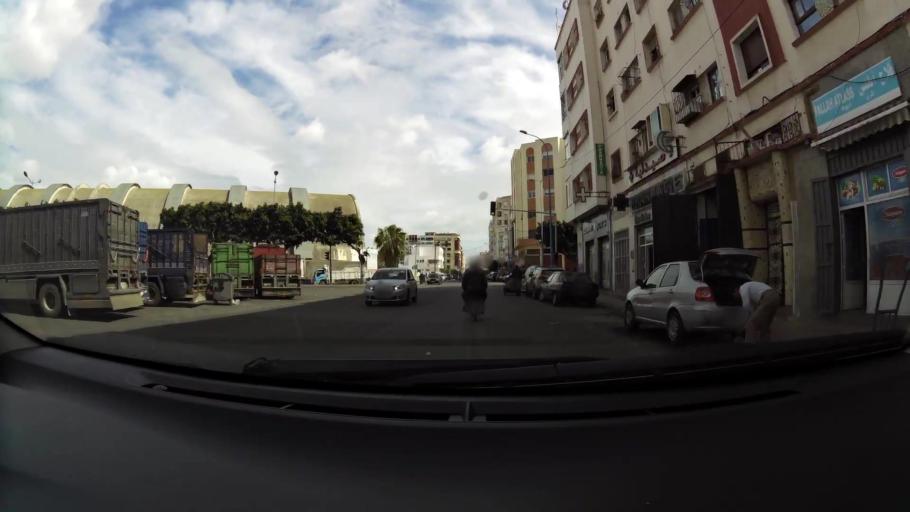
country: MA
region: Grand Casablanca
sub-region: Casablanca
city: Casablanca
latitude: 33.5898
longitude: -7.5963
